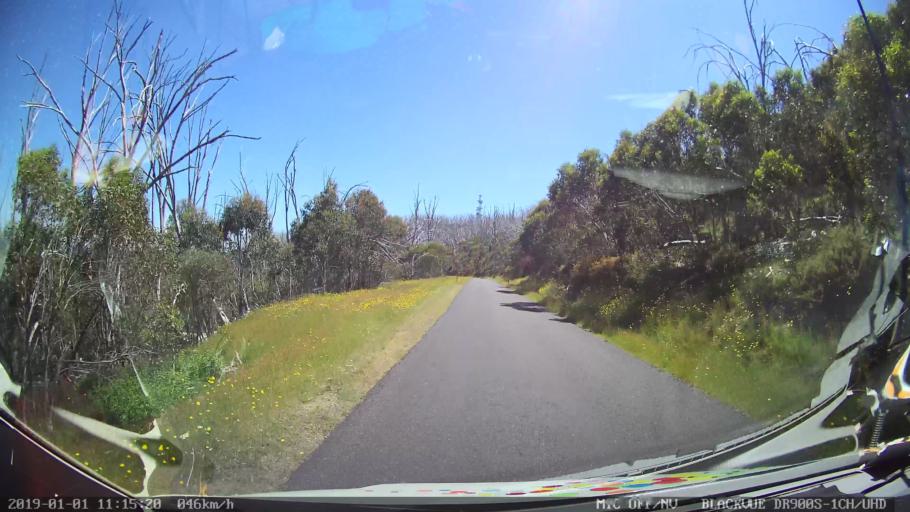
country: AU
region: New South Wales
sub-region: Snowy River
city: Jindabyne
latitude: -35.9457
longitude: 148.3867
